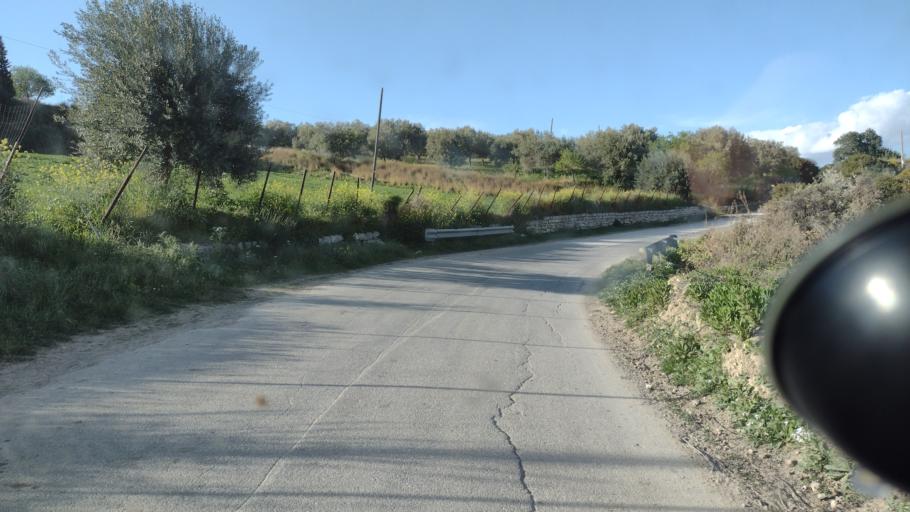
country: IT
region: Sicily
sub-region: Provincia di Siracusa
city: Noto
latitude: 36.8591
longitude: 15.0237
